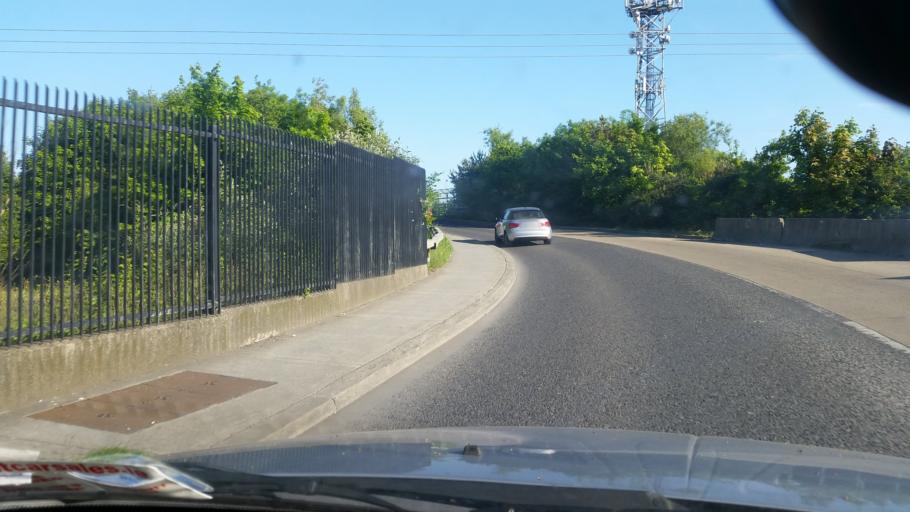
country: IE
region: Leinster
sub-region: Dublin City
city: Finglas
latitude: 53.3979
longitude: -6.3322
